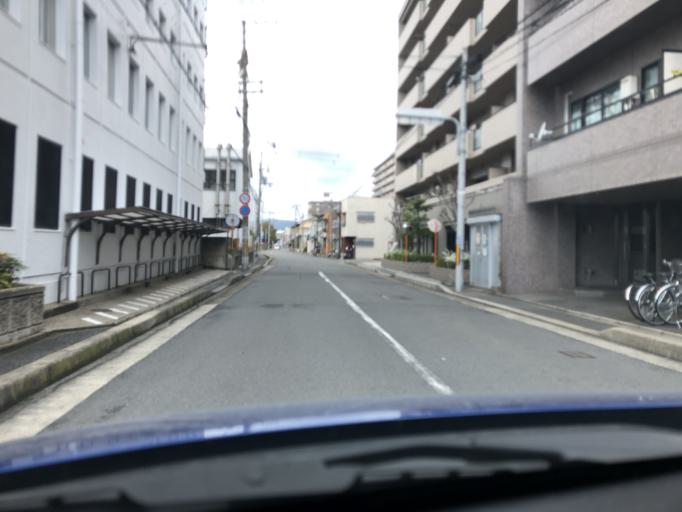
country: JP
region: Kyoto
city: Kyoto
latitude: 34.9988
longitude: 135.7460
